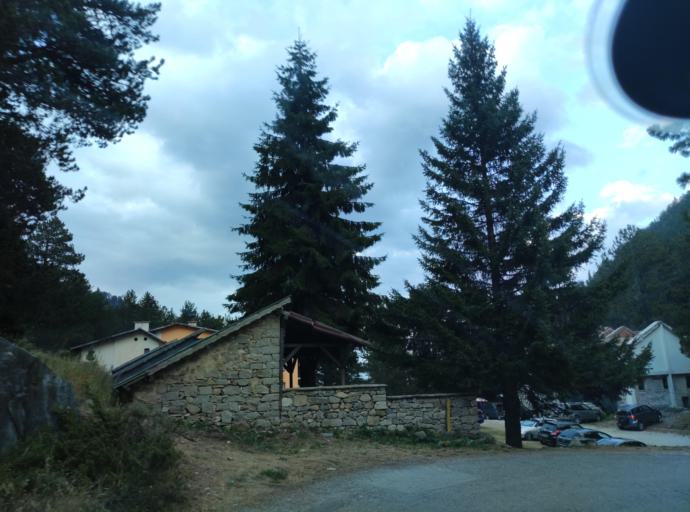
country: BG
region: Blagoevgrad
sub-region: Obshtina Bansko
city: Bansko
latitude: 41.7683
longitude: 23.4262
